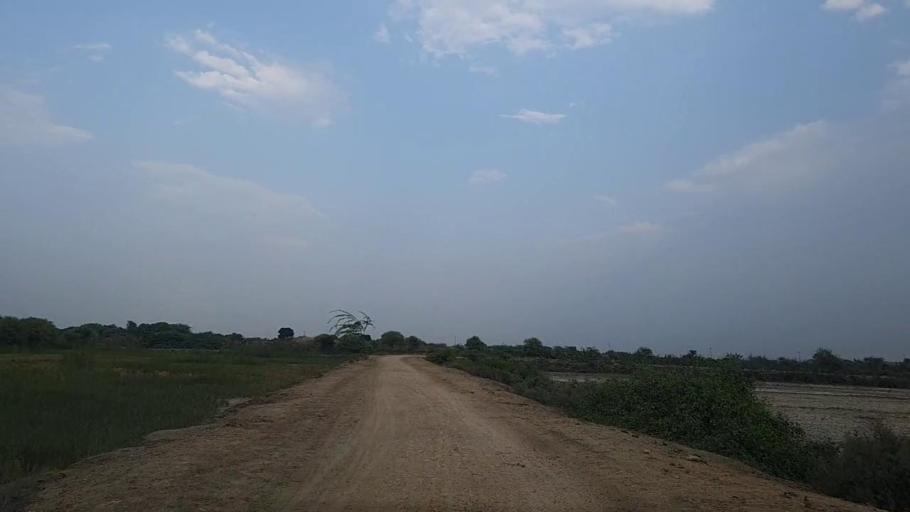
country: PK
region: Sindh
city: Daro Mehar
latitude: 24.7718
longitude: 68.1526
